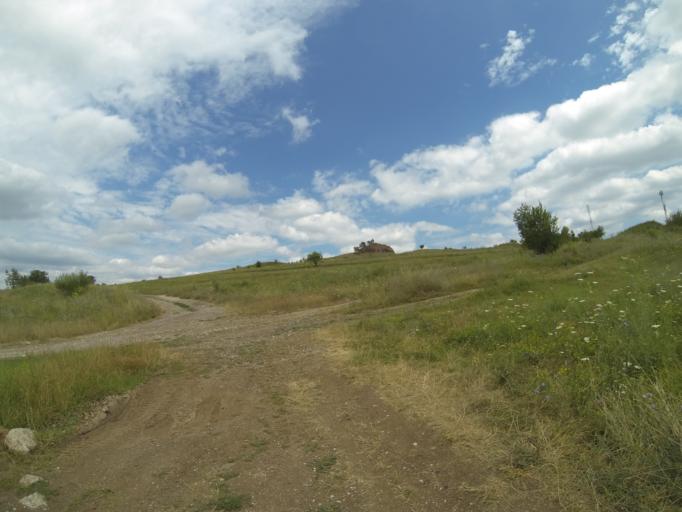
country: RO
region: Brasov
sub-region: Comuna Apata
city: Apata
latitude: 46.0291
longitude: 25.4181
